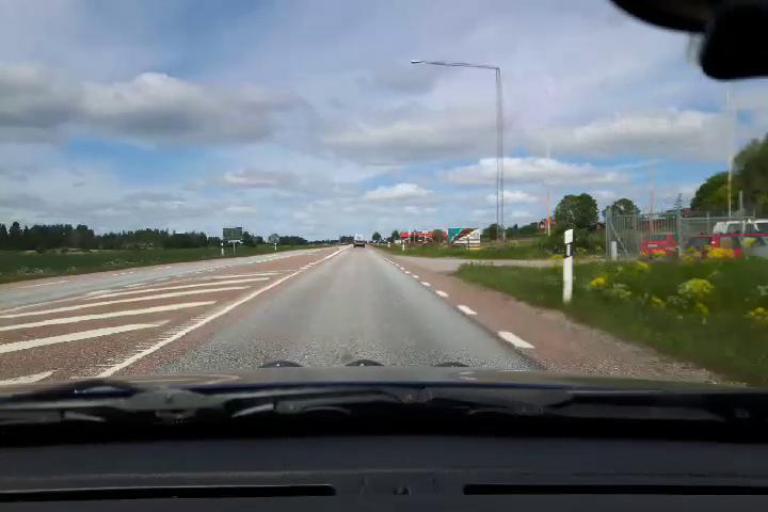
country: SE
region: Uppsala
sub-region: Uppsala Kommun
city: Gamla Uppsala
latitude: 59.9346
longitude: 17.5959
